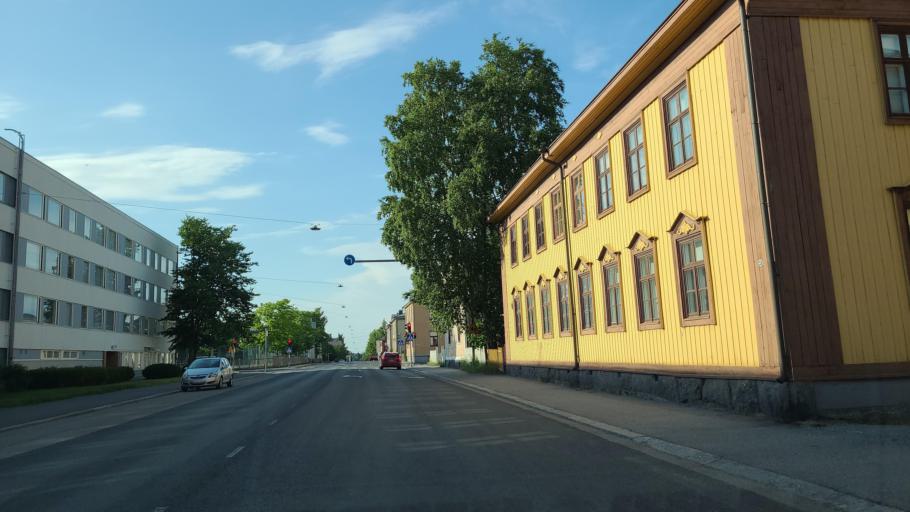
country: FI
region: Ostrobothnia
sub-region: Vaasa
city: Vaasa
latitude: 63.1002
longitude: 21.6218
